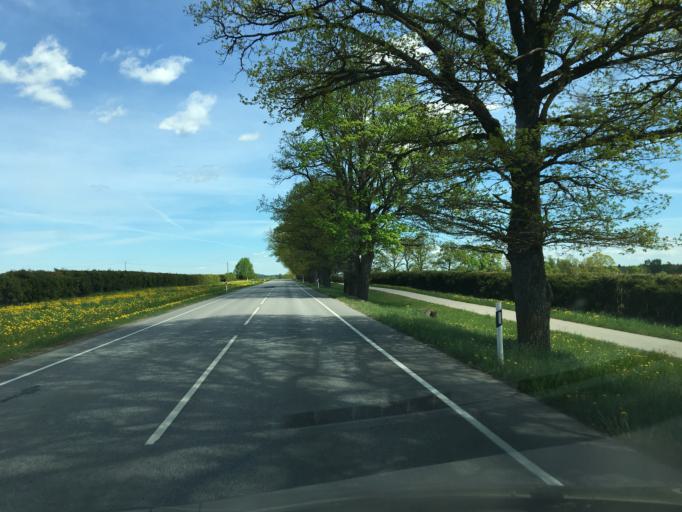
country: EE
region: Vorumaa
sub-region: Antsla vald
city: Vana-Antsla
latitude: 57.9179
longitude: 26.3104
